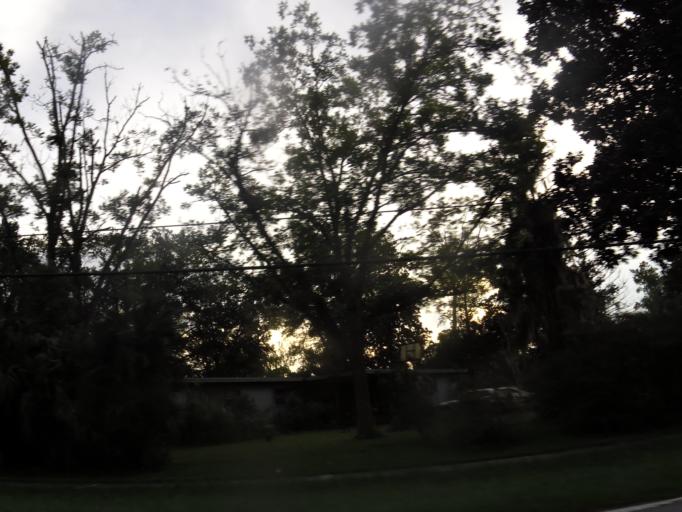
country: US
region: Florida
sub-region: Clay County
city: Bellair-Meadowbrook Terrace
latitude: 30.2906
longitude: -81.7813
